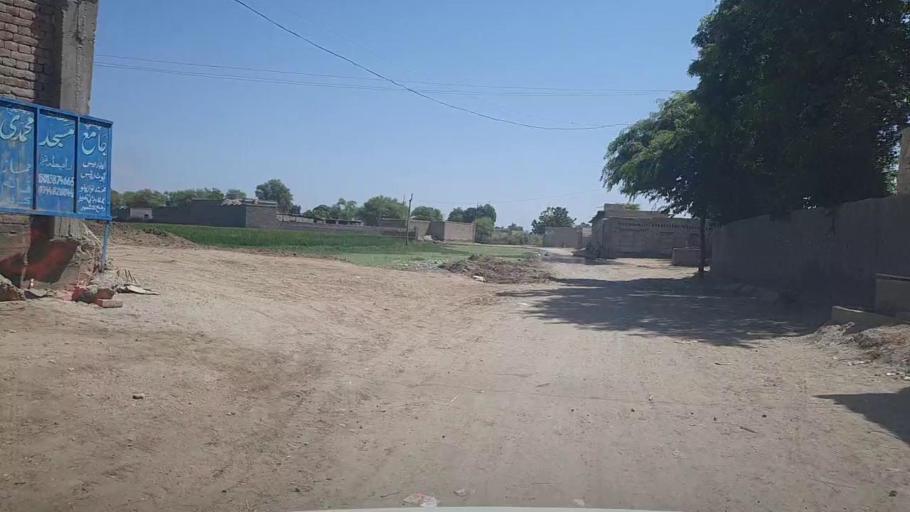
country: PK
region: Sindh
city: Kashmor
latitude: 28.2999
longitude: 69.4249
